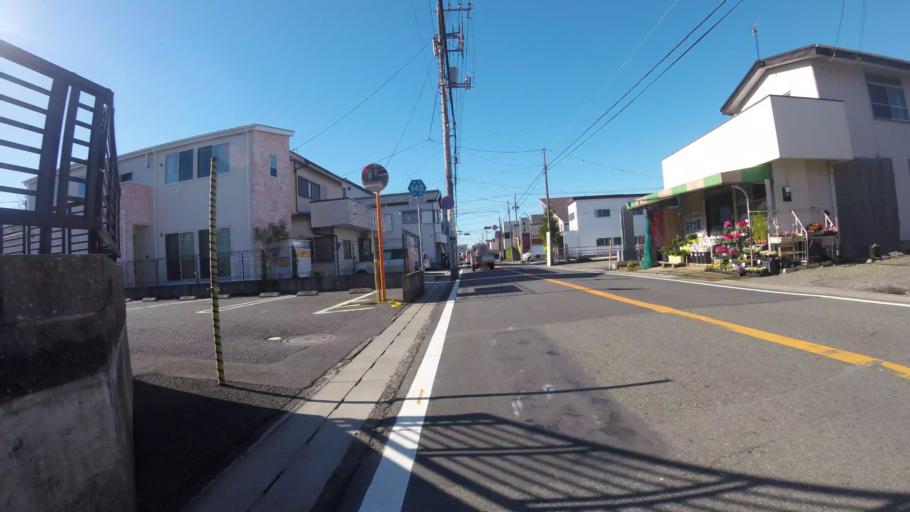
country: JP
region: Shizuoka
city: Mishima
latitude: 35.1167
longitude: 138.9071
